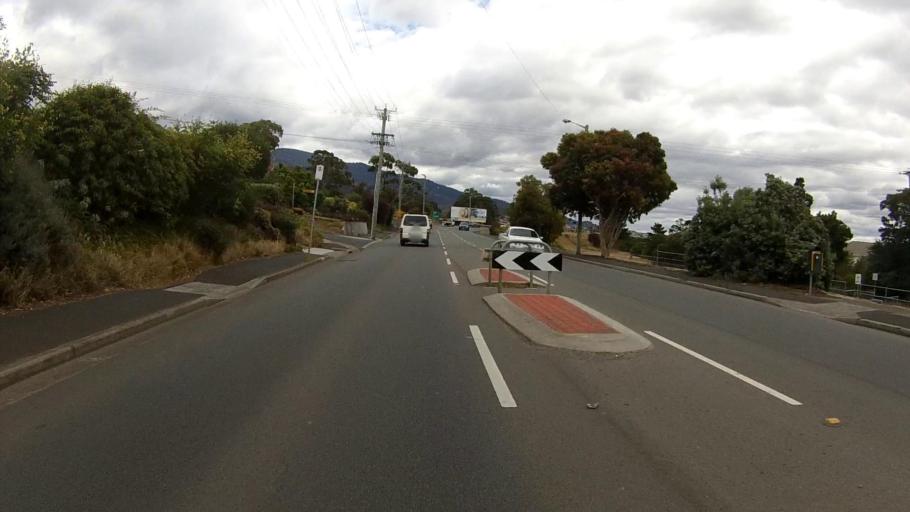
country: AU
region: Tasmania
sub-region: Glenorchy
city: Berriedale
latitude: -42.8209
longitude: 147.2624
